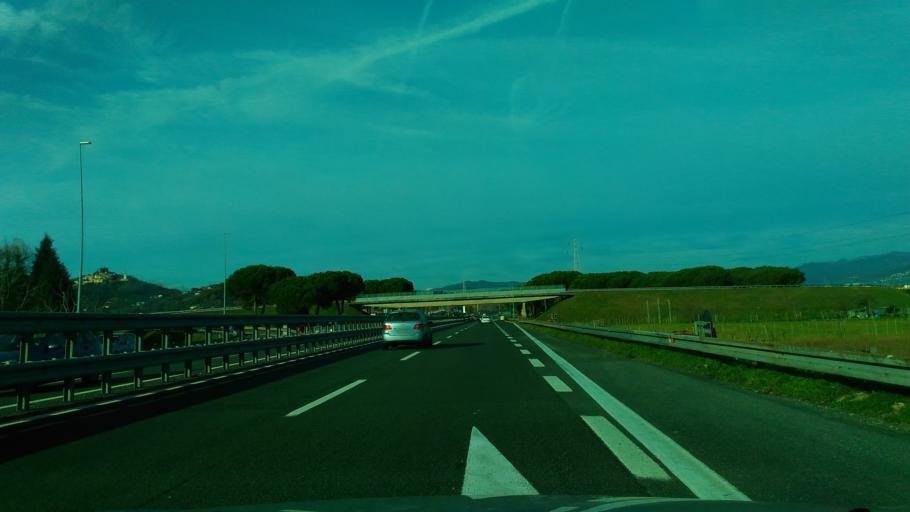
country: IT
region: Liguria
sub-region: Provincia di La Spezia
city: Sarzana
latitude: 44.0999
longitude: 9.9553
